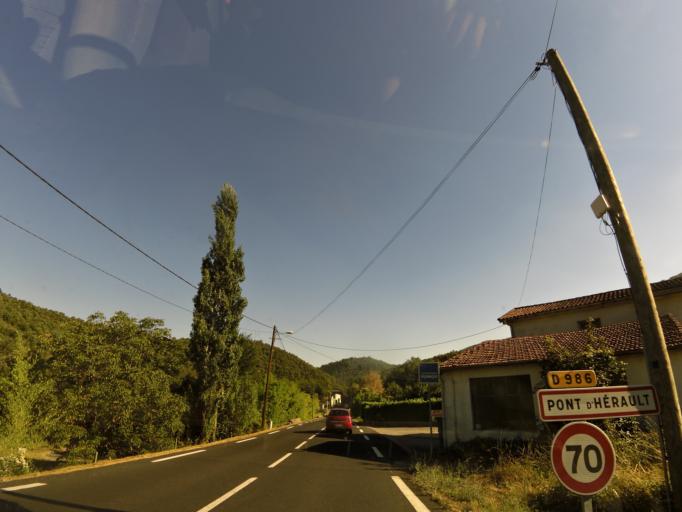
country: FR
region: Languedoc-Roussillon
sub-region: Departement du Gard
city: Sumene
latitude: 44.0004
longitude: 3.6757
